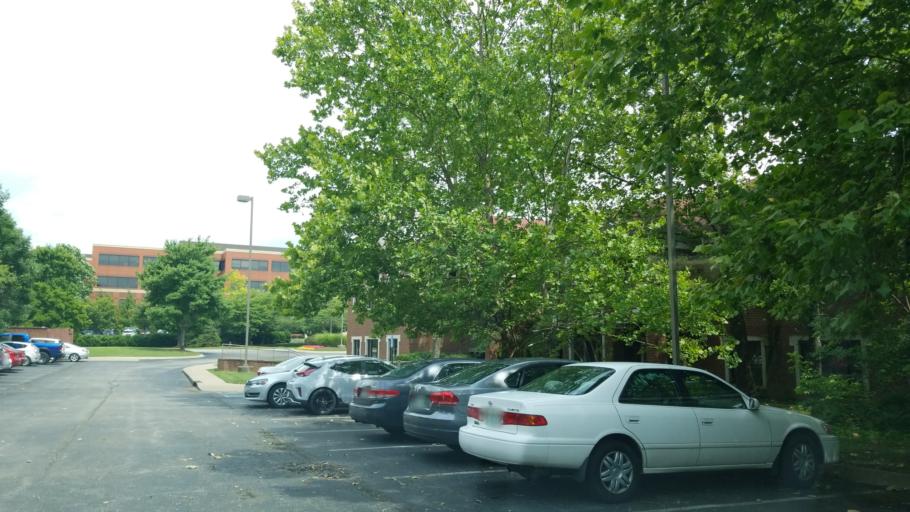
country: US
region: Tennessee
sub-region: Williamson County
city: Brentwood
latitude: 36.0336
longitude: -86.8098
